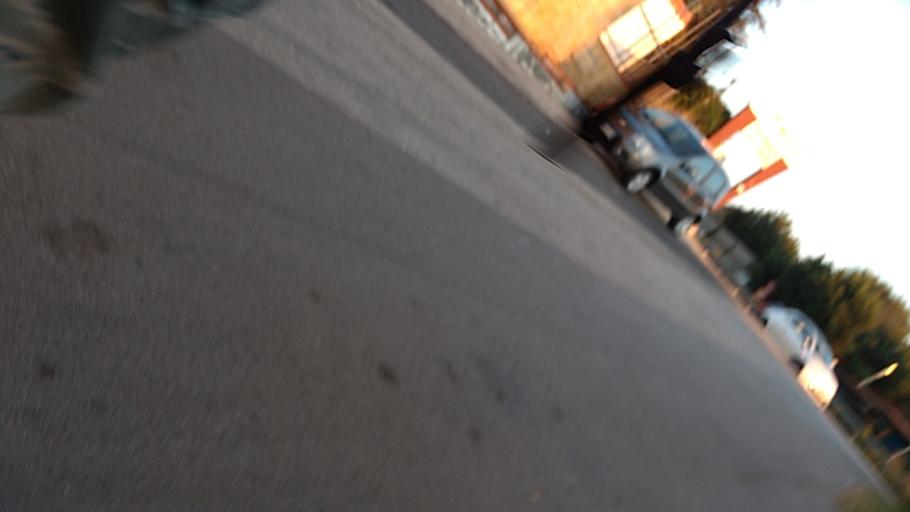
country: IT
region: Campania
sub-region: Provincia di Napoli
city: Masseria Vecchia Ovest
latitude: 40.9347
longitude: 14.0472
